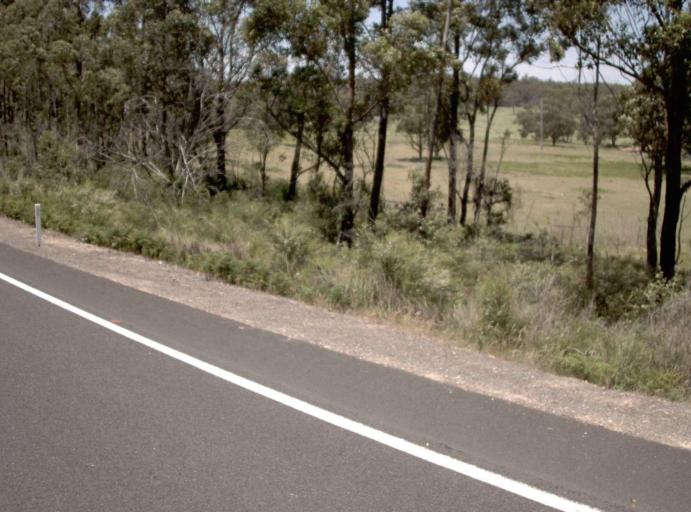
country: AU
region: Victoria
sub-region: East Gippsland
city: Lakes Entrance
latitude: -37.7518
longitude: 148.2904
